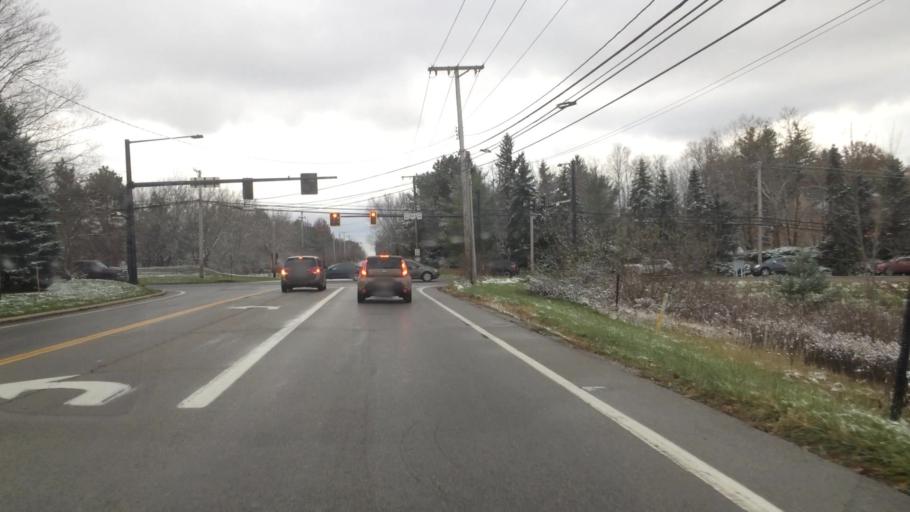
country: US
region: Ohio
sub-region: Summit County
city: Hudson
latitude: 41.2405
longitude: -81.4112
